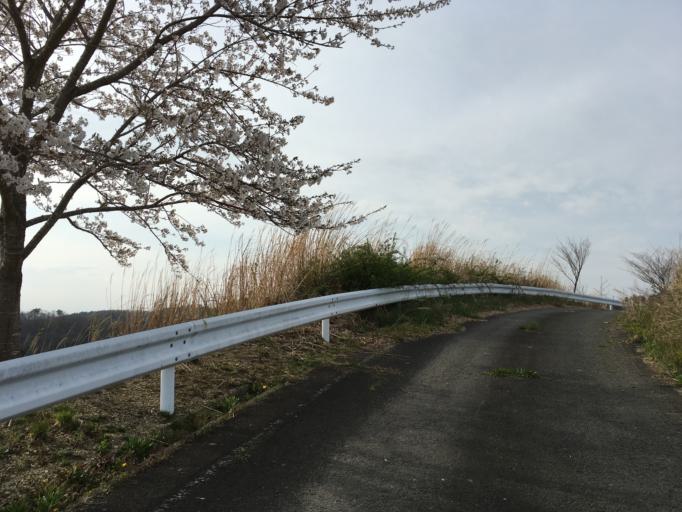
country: JP
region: Iwate
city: Ichinoseki
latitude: 38.8215
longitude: 141.2930
